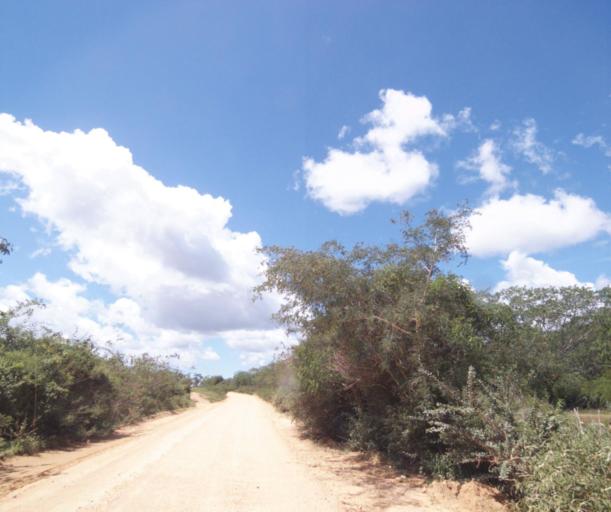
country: BR
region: Bahia
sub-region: Pocoes
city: Pocoes
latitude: -14.3411
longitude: -40.5939
